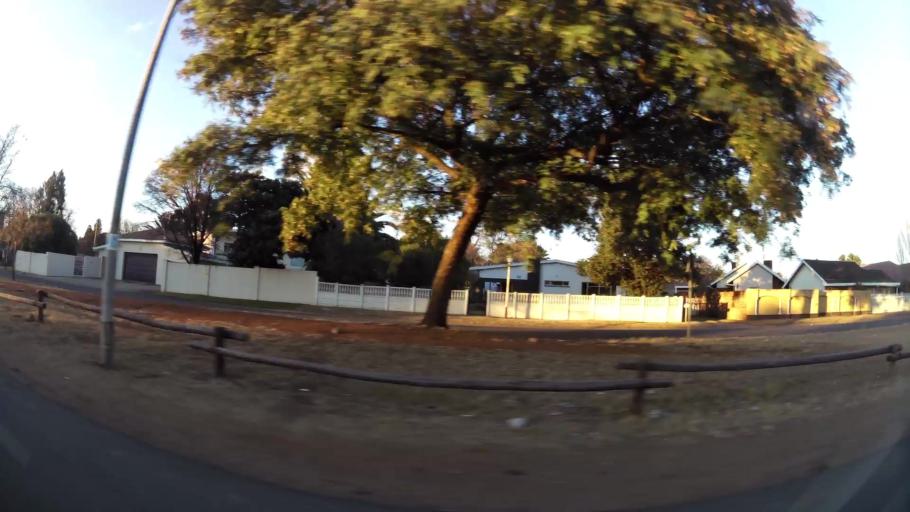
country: ZA
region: North-West
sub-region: Dr Kenneth Kaunda District Municipality
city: Potchefstroom
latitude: -26.7146
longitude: 27.1125
